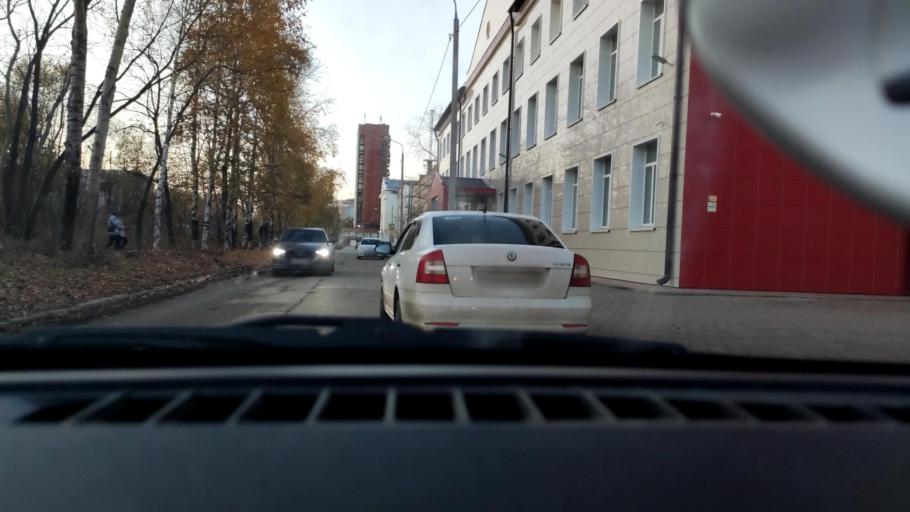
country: RU
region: Perm
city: Perm
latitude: 58.0158
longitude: 56.2758
